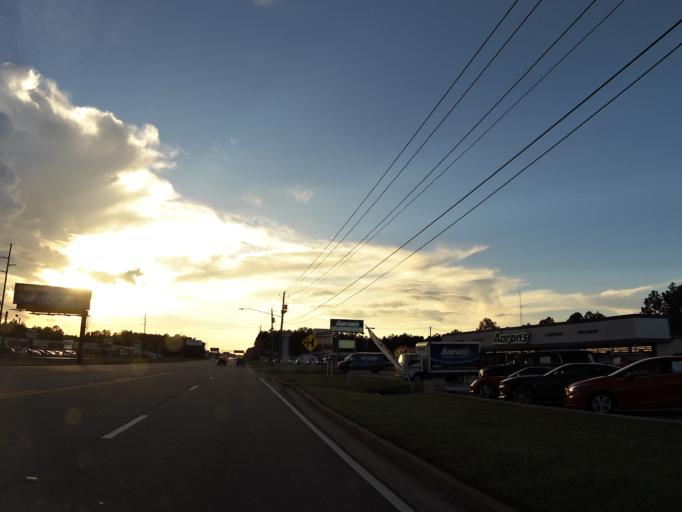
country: US
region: Georgia
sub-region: Camden County
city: St Marys
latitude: 30.7810
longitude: -81.6278
